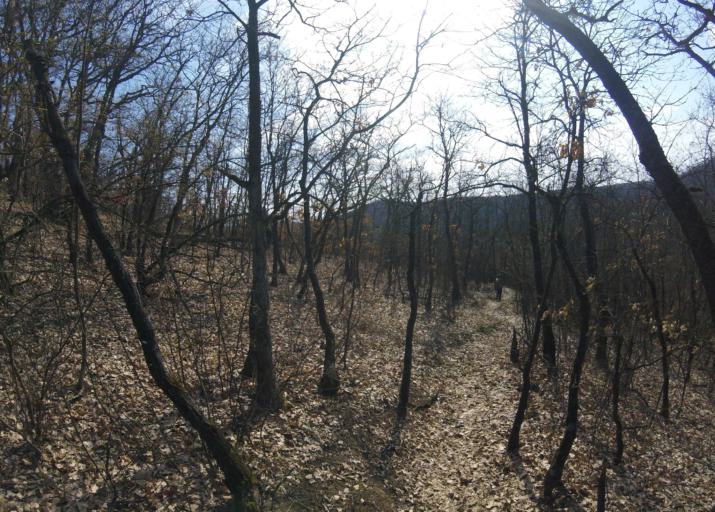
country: HU
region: Heves
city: Belapatfalva
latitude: 47.9930
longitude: 20.3304
